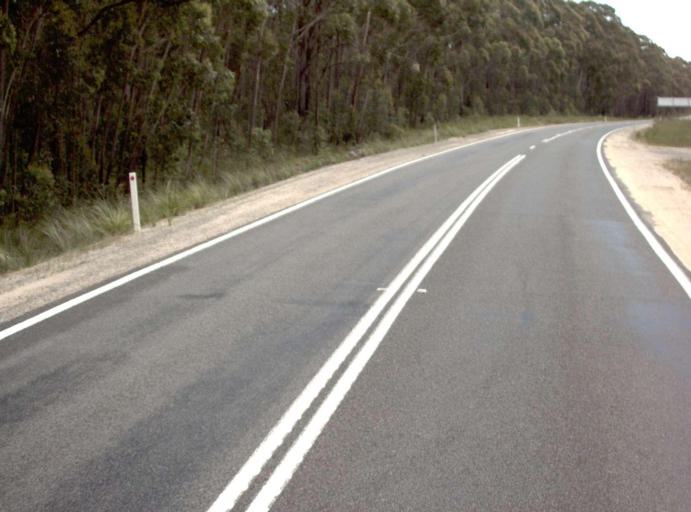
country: AU
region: New South Wales
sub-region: Bega Valley
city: Eden
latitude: -37.5373
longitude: 149.4743
